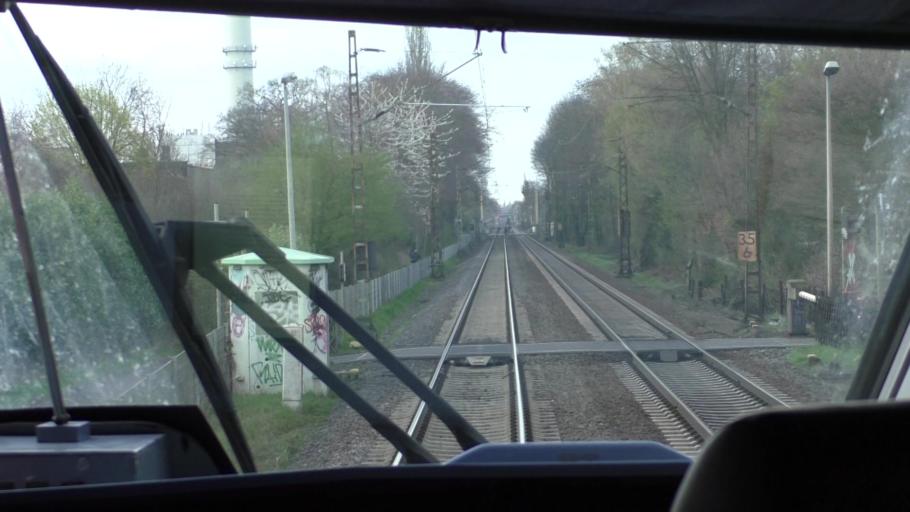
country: DE
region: North Rhine-Westphalia
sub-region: Regierungsbezirk Koln
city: Bonn
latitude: 50.7052
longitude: 7.1274
